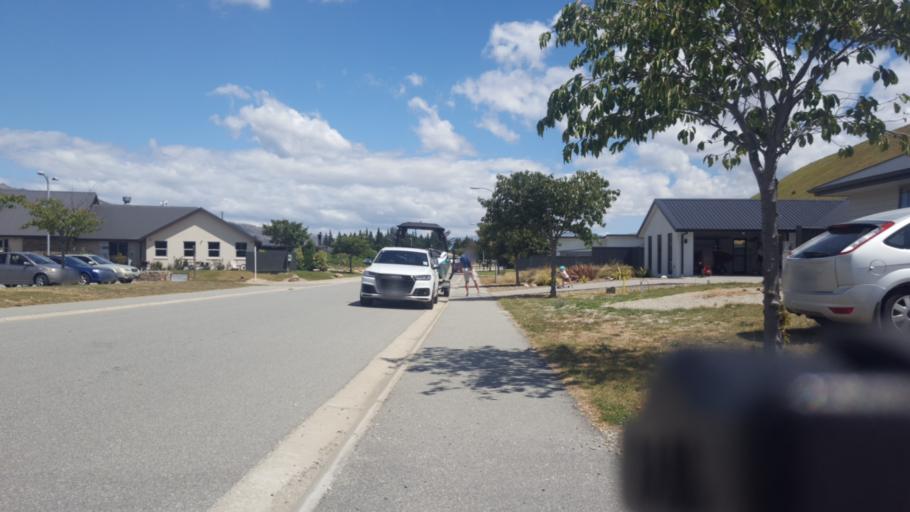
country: NZ
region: Otago
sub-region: Queenstown-Lakes District
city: Wanaka
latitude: -44.9802
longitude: 169.2354
